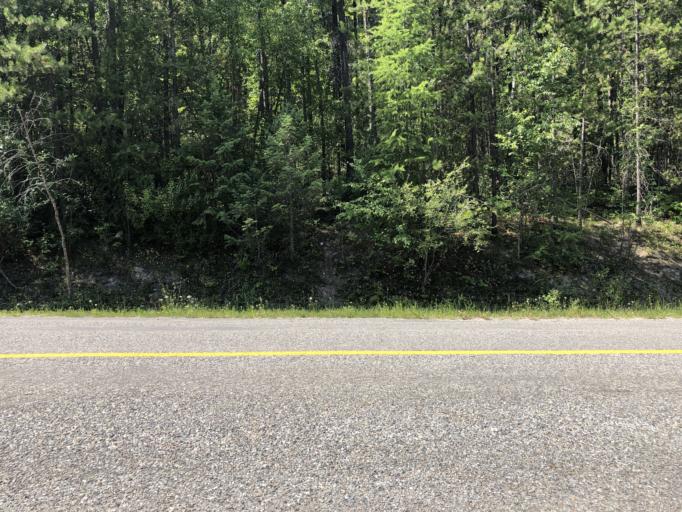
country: CA
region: British Columbia
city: Fernie
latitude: 49.4130
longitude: -115.3109
